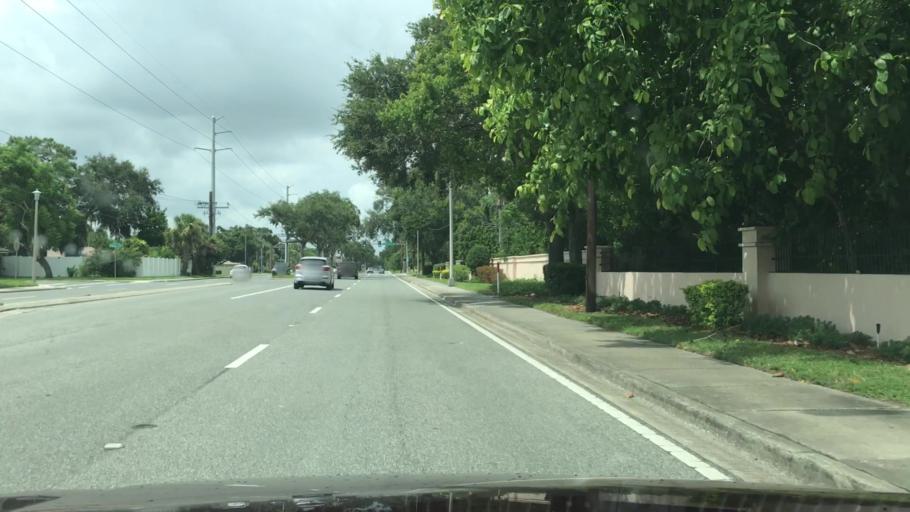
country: US
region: Florida
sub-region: Sarasota County
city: Gulf Gate Estates
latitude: 27.2437
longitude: -82.4975
